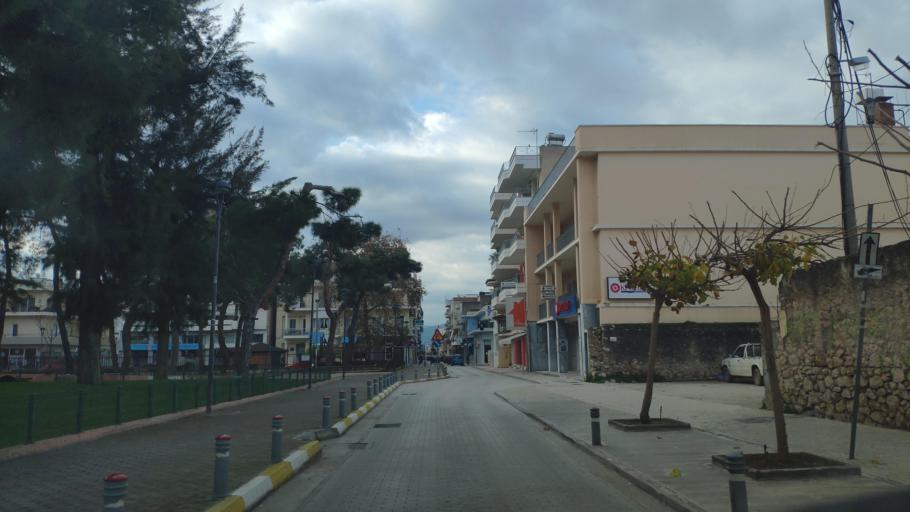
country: GR
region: Peloponnese
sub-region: Nomos Argolidos
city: Argos
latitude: 37.6342
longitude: 22.7257
